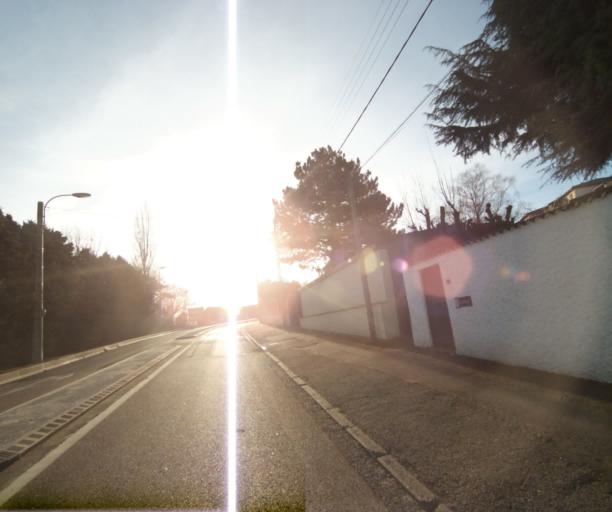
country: FR
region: Lorraine
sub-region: Departement de Meurthe-et-Moselle
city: Villers-les-Nancy
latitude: 48.6618
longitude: 6.1647
